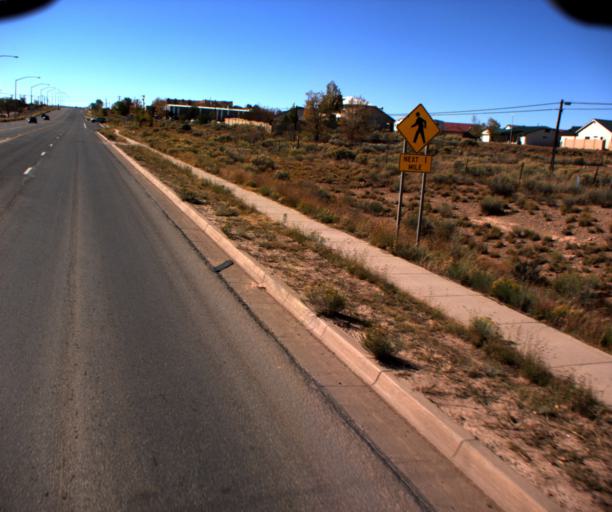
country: US
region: Arizona
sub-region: Apache County
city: Saint Michaels
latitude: 35.6572
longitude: -109.0900
